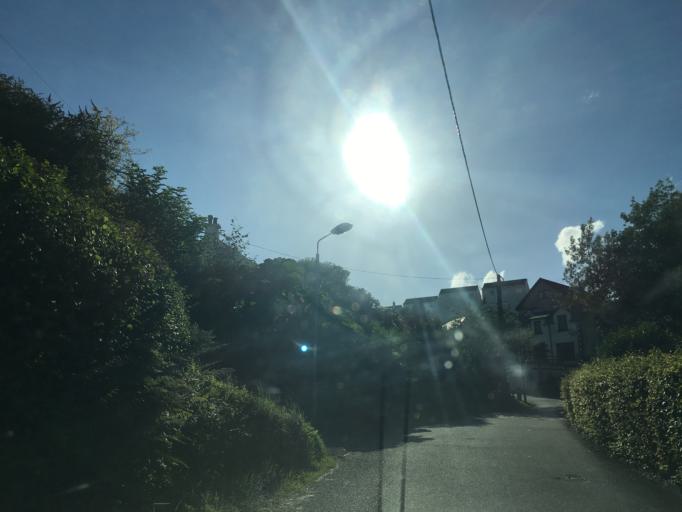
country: GB
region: Scotland
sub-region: Argyll and Bute
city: Oban
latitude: 56.4085
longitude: -5.4795
